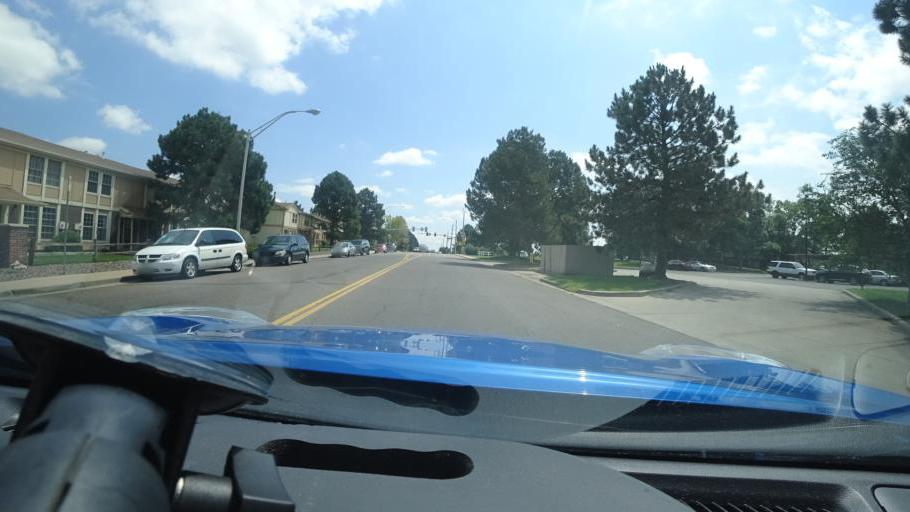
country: US
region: Colorado
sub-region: Adams County
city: Aurora
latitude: 39.7184
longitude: -104.8486
